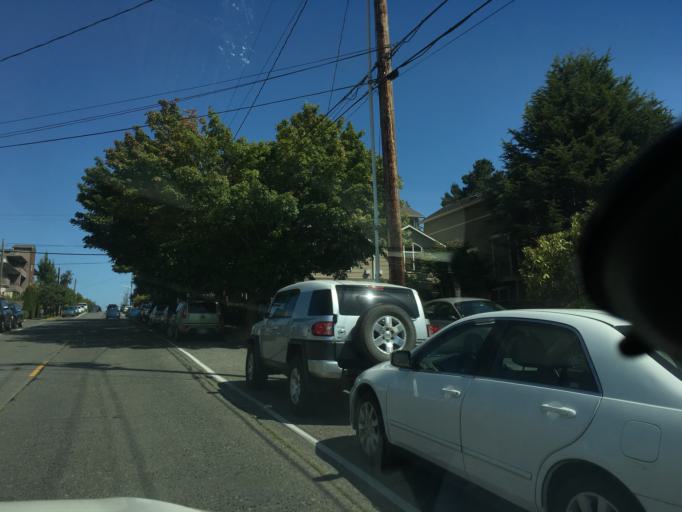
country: US
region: Washington
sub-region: King County
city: Shoreline
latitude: 47.6906
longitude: -122.3940
